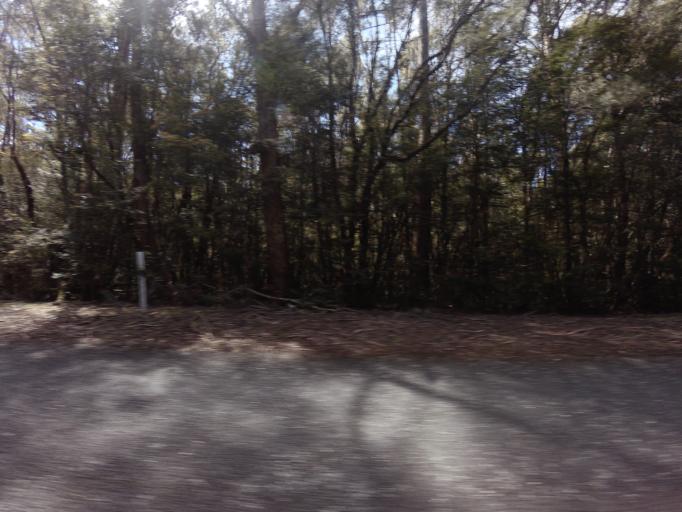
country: AU
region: Tasmania
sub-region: West Coast
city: Queenstown
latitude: -42.8020
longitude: 146.0957
